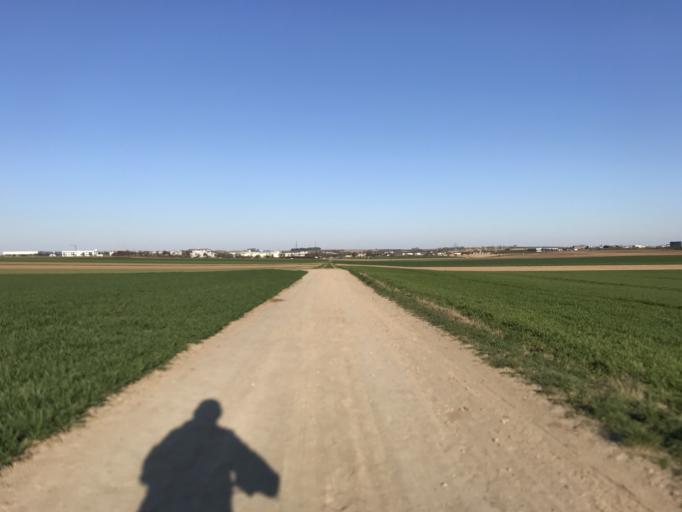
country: DE
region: Rheinland-Pfalz
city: Klein-Winternheim
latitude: 49.9526
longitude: 8.2402
